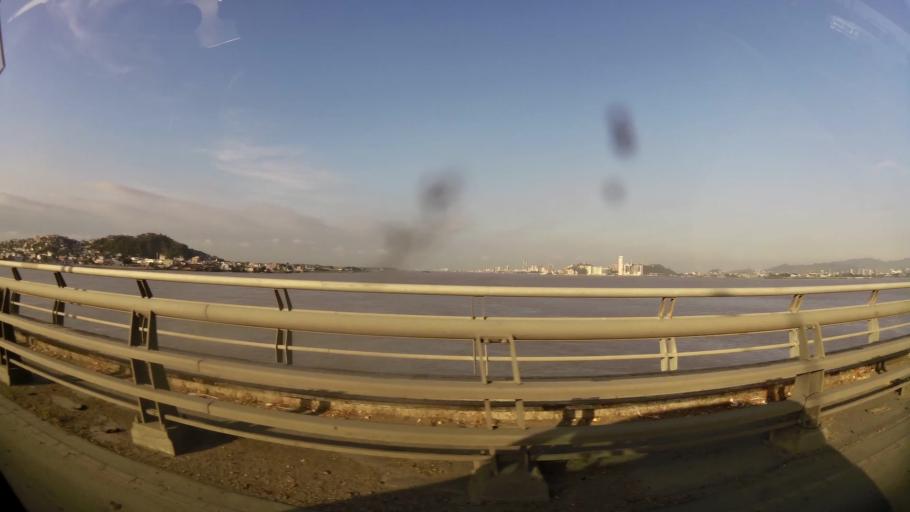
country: EC
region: Guayas
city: Eloy Alfaro
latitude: -2.1606
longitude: -79.8525
